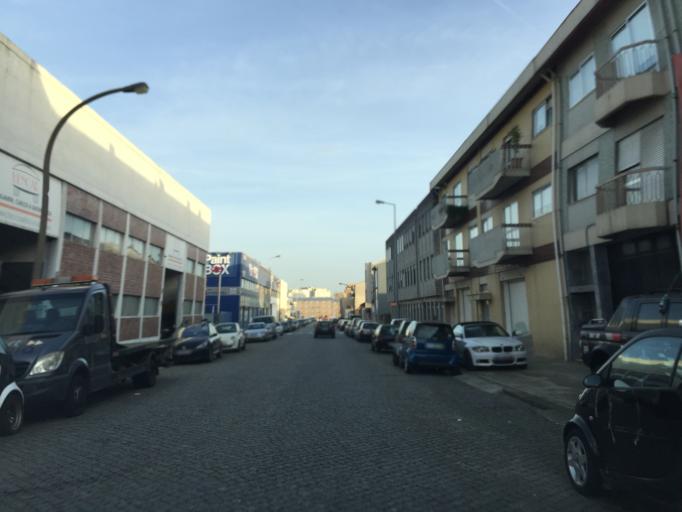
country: PT
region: Porto
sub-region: Matosinhos
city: Senhora da Hora
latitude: 41.1721
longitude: -8.6516
